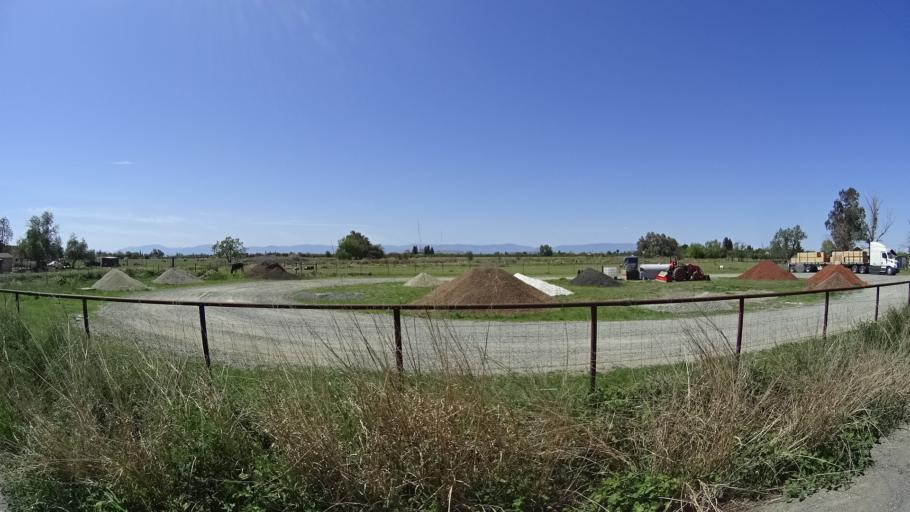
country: US
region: California
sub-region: Glenn County
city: Orland
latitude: 39.7437
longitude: -122.1502
